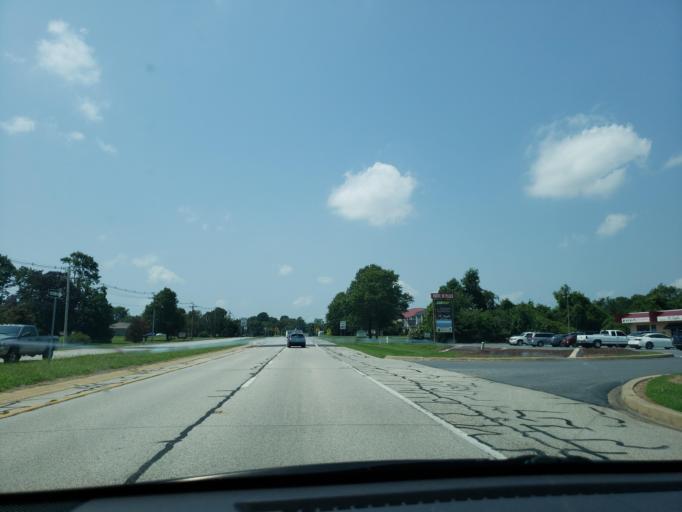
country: US
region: Delaware
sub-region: Kent County
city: Highland Acres
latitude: 39.1182
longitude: -75.5104
